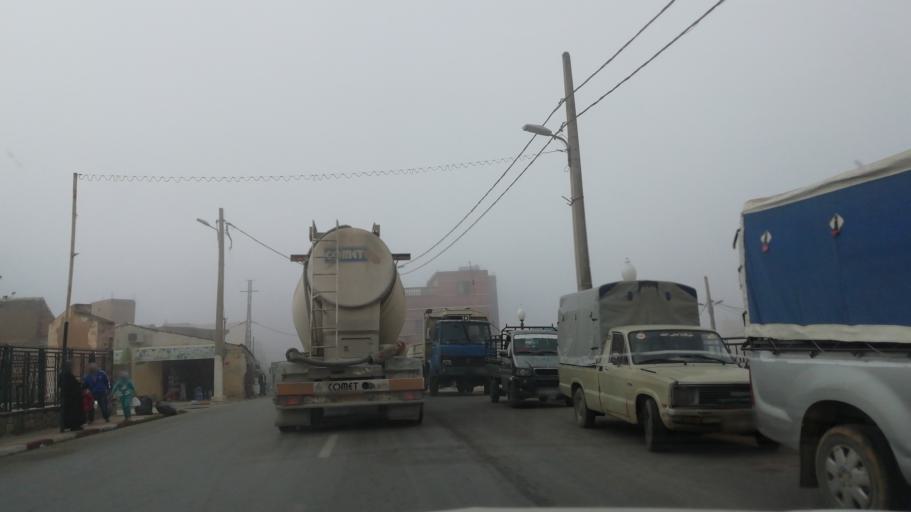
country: DZ
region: Mascara
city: Mascara
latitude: 35.5178
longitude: 0.3057
